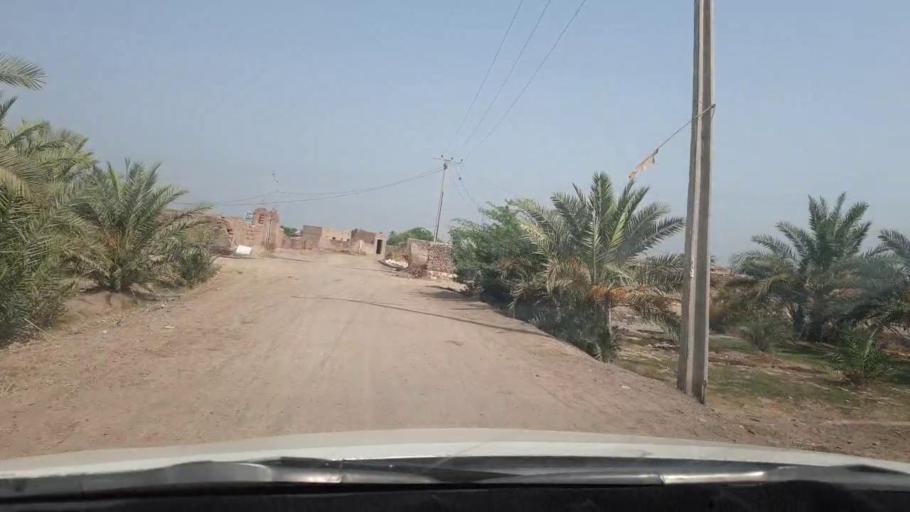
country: PK
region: Sindh
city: Rohri
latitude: 27.6282
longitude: 68.8870
